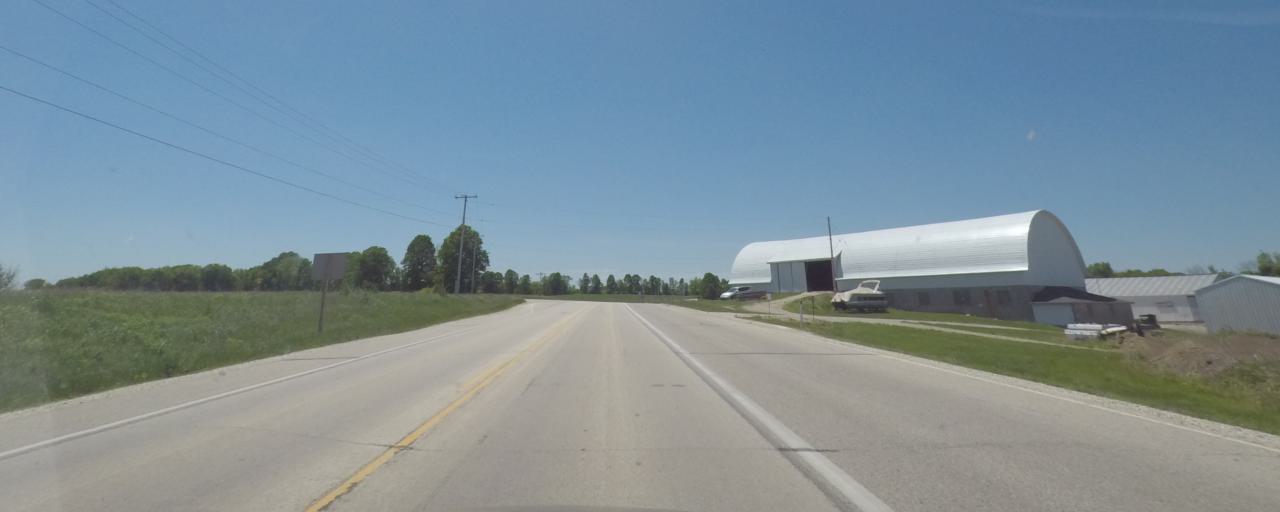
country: US
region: Wisconsin
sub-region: Ozaukee County
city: Kohler
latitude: 43.5135
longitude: -88.1149
